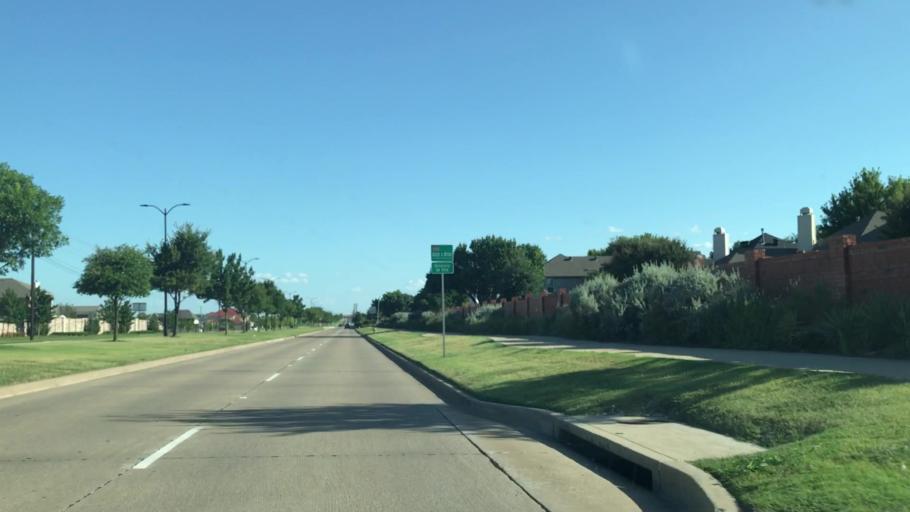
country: US
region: Texas
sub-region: Collin County
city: Frisco
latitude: 33.1289
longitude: -96.7681
